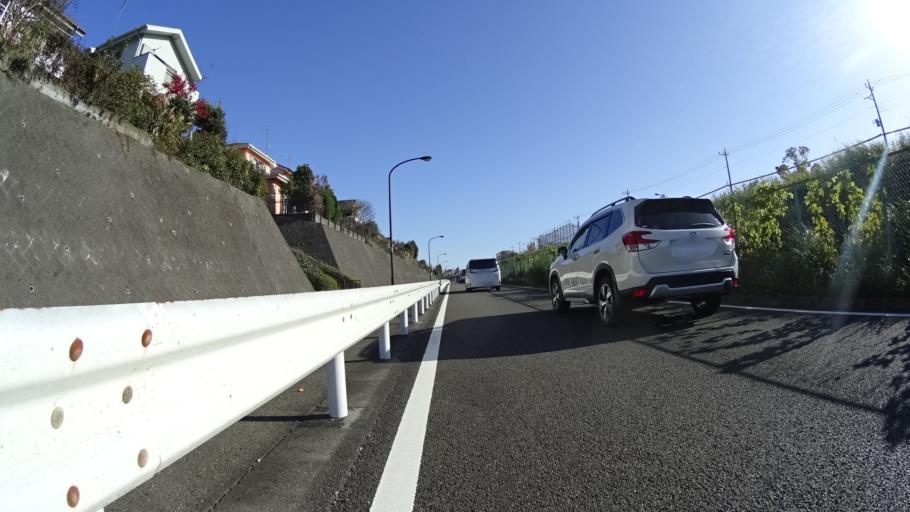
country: JP
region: Tokyo
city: Hino
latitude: 35.6117
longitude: 139.4185
